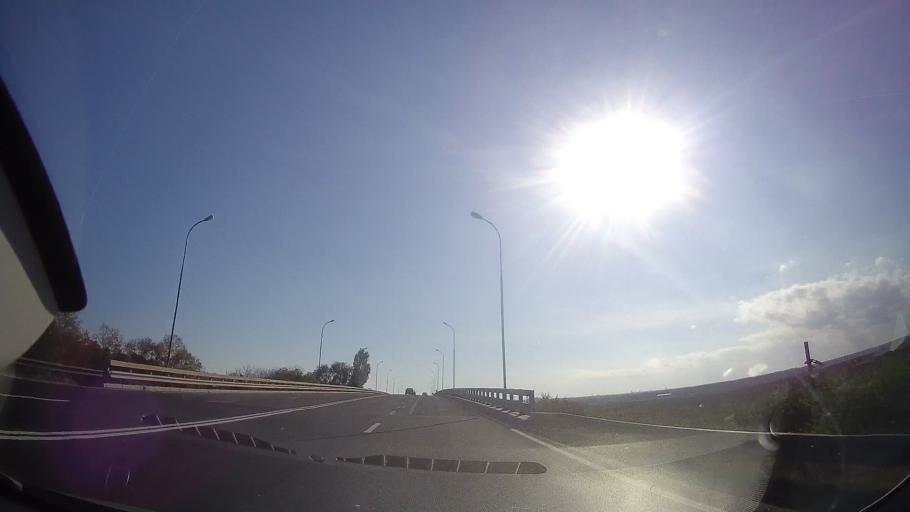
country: RO
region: Constanta
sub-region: Comuna Douazeci si Trei August
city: Dulcesti
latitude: 43.8596
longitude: 28.5756
